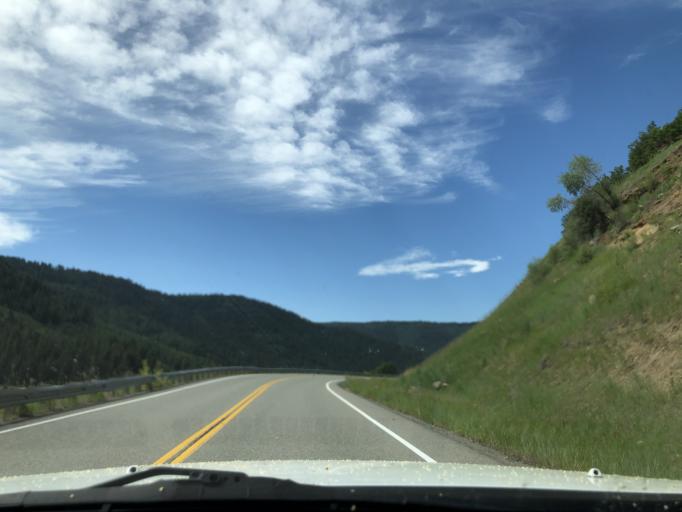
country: US
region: Colorado
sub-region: Delta County
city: Paonia
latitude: 38.9601
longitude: -107.3391
